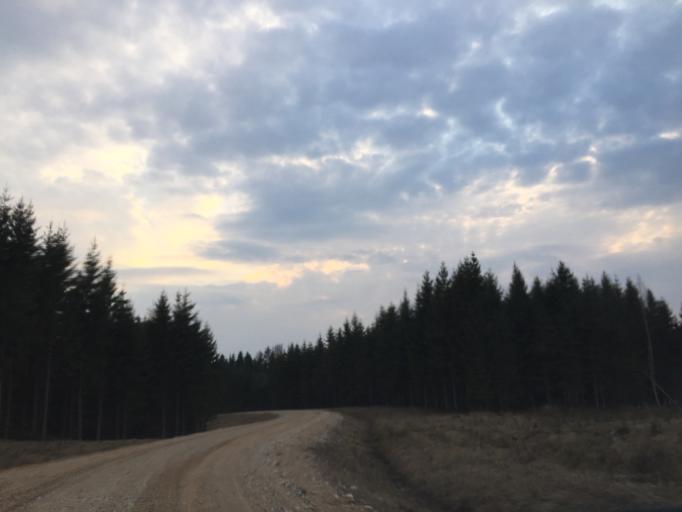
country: LV
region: Raunas
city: Rauna
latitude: 57.1185
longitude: 25.5982
